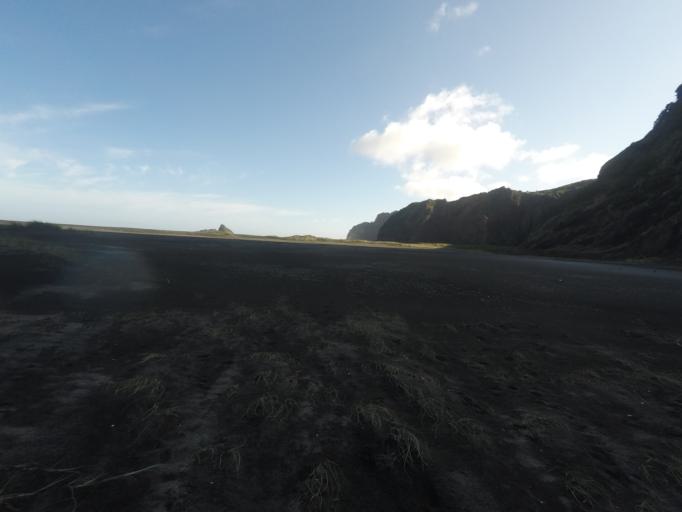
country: NZ
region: Auckland
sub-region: Auckland
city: Muriwai Beach
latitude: -36.9994
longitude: 174.4760
